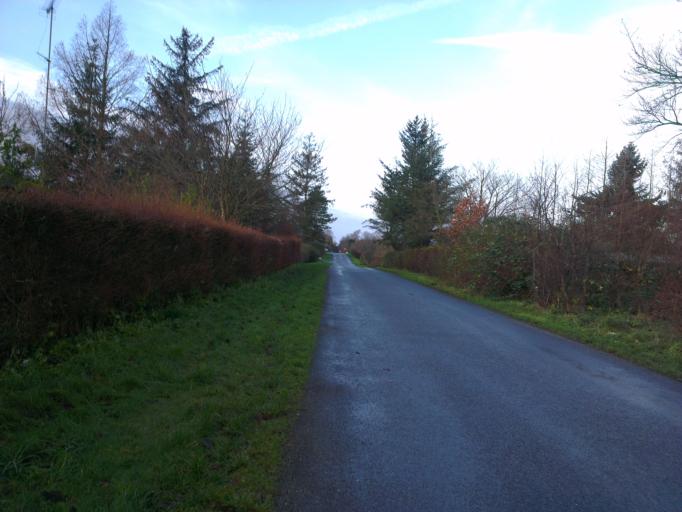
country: DK
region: Capital Region
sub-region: Frederikssund Kommune
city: Jaegerspris
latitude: 55.8394
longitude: 11.9644
